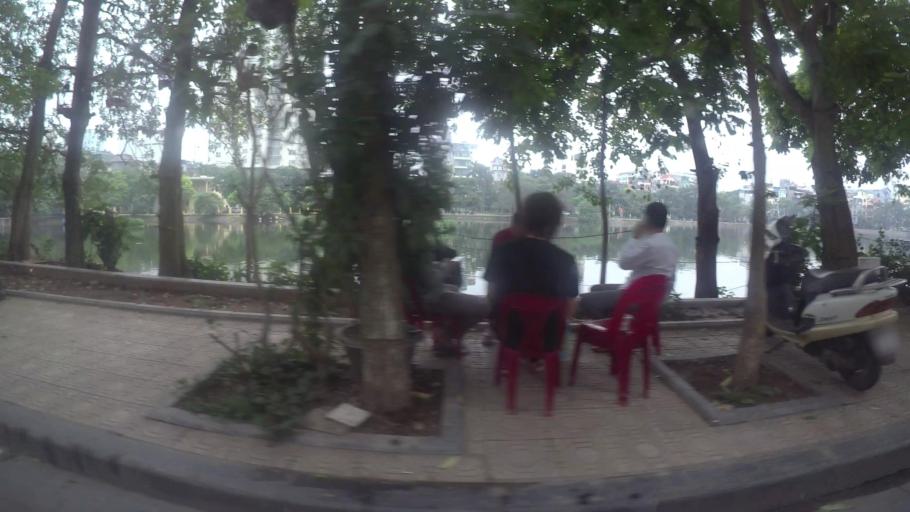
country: VN
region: Ha Noi
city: Hoan Kiem
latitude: 21.0446
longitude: 105.8408
